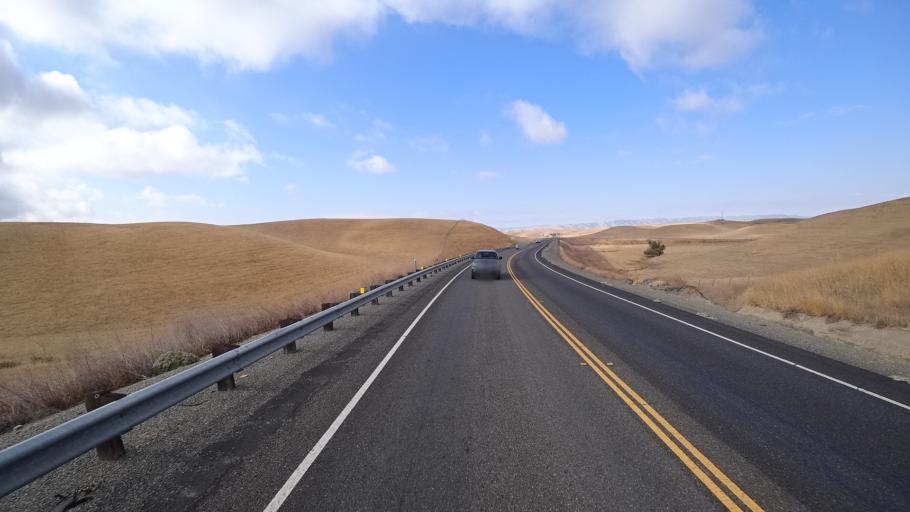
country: US
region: California
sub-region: Yolo County
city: Dunnigan
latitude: 38.7779
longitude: -121.9398
